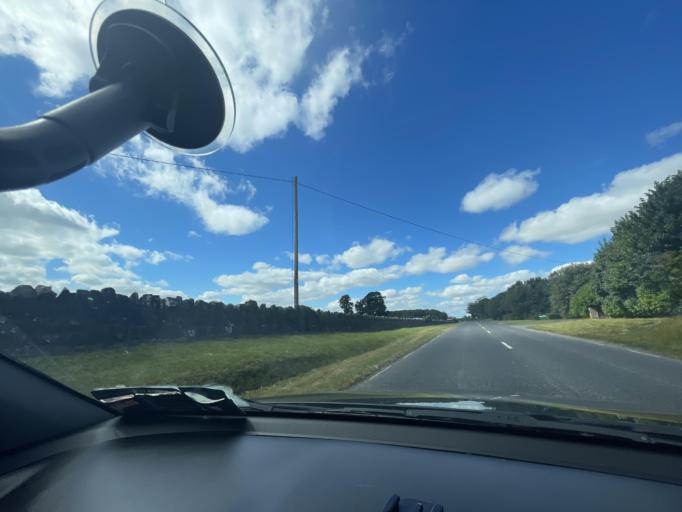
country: IE
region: Leinster
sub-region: An Mhi
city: Dunshaughlin
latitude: 53.5227
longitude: -6.6556
